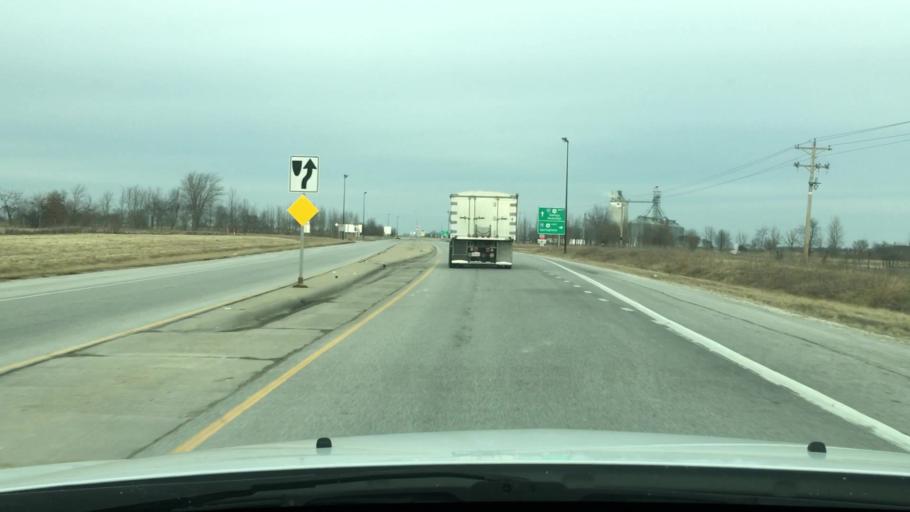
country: US
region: Illinois
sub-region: Pike County
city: Griggsville
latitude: 39.6712
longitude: -90.7692
